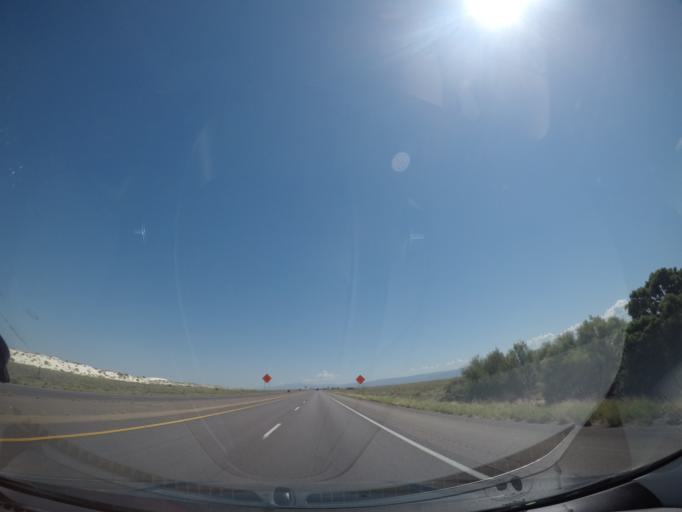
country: US
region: New Mexico
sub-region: Otero County
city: Holloman Air Force Base
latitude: 32.7688
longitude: -106.1804
